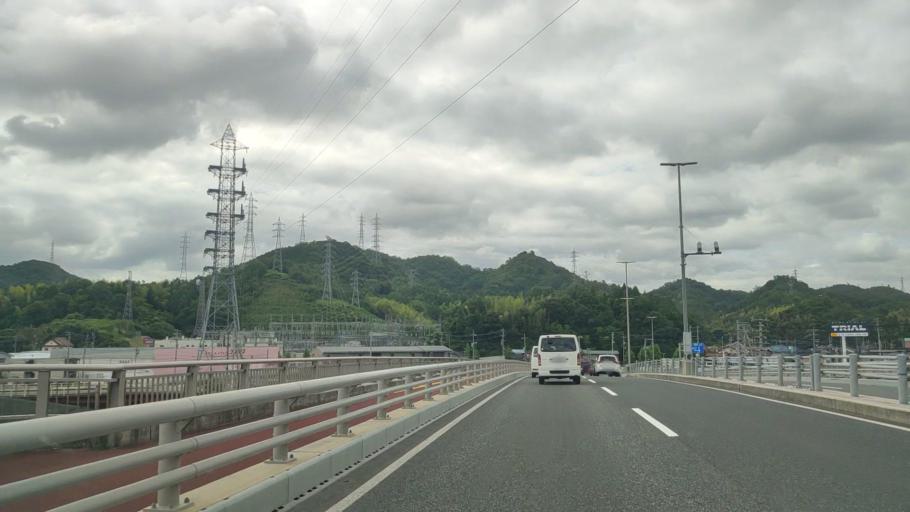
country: JP
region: Tottori
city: Yonago
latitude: 35.4201
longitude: 133.3345
